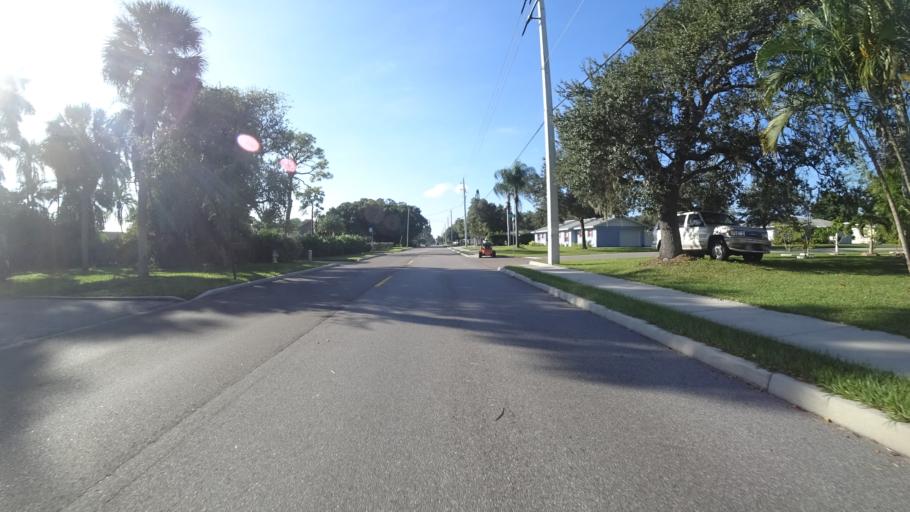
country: US
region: Florida
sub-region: Manatee County
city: West Bradenton
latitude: 27.4901
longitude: -82.6122
